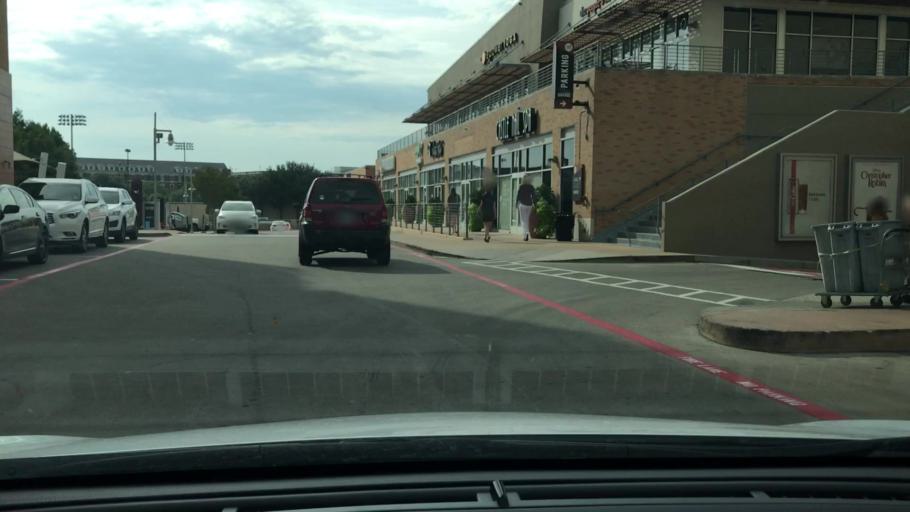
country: US
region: Texas
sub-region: Dallas County
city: Highland Park
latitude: 32.8380
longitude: -96.7759
